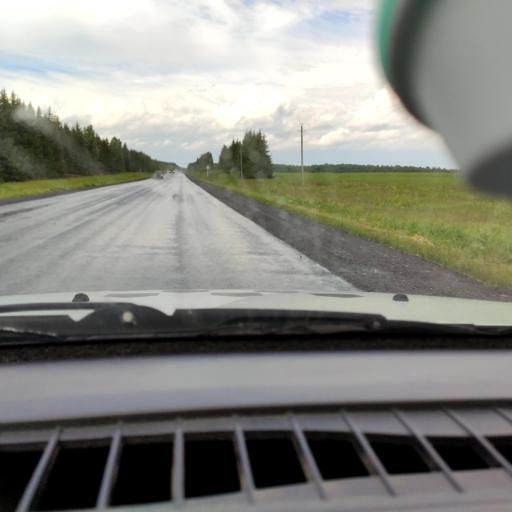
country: RU
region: Perm
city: Orda
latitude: 57.2137
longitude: 56.9392
